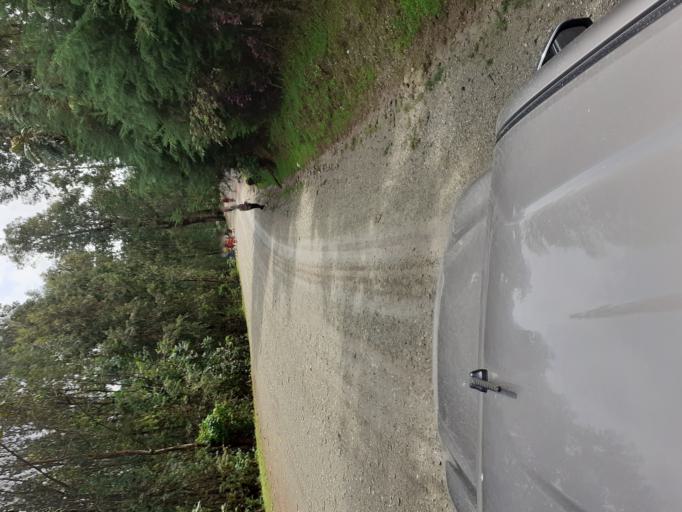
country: ET
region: Oromiya
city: Gimbi
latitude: 9.2786
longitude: 35.6906
